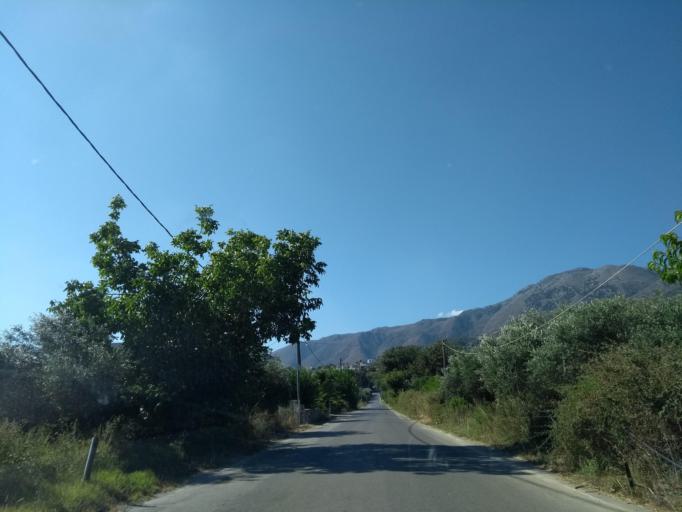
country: GR
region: Crete
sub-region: Nomos Chanias
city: Georgioupolis
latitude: 35.3367
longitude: 24.2796
